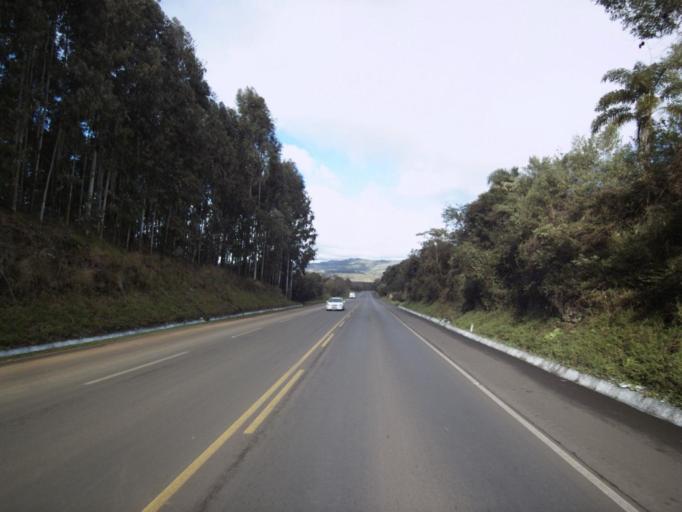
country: BR
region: Santa Catarina
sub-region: Concordia
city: Concordia
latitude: -27.1120
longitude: -51.9100
